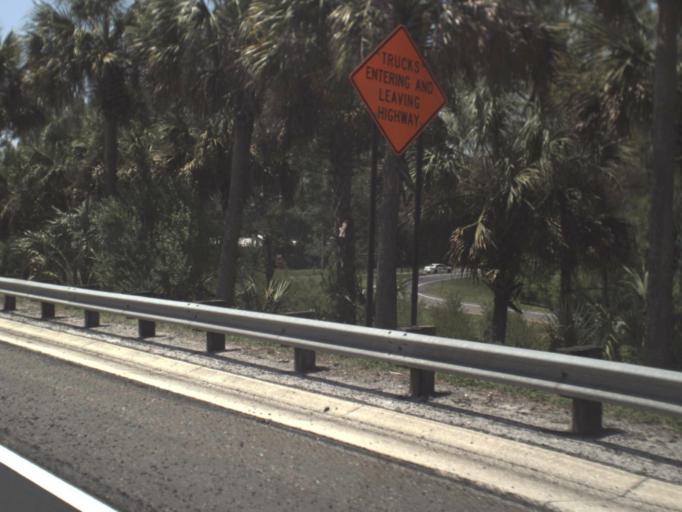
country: US
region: Florida
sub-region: Nassau County
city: Yulee
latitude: 30.5187
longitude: -81.6354
